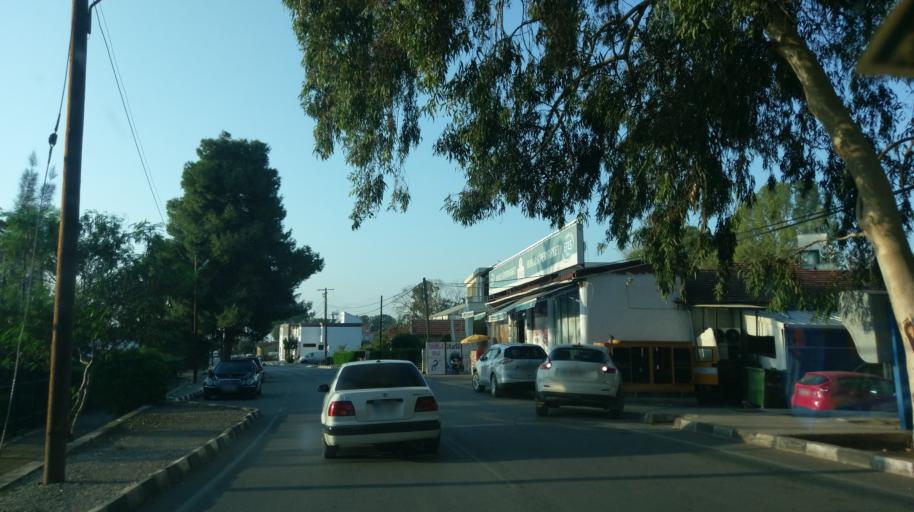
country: CY
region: Lefkosia
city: Astromeritis
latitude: 35.1654
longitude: 33.0124
